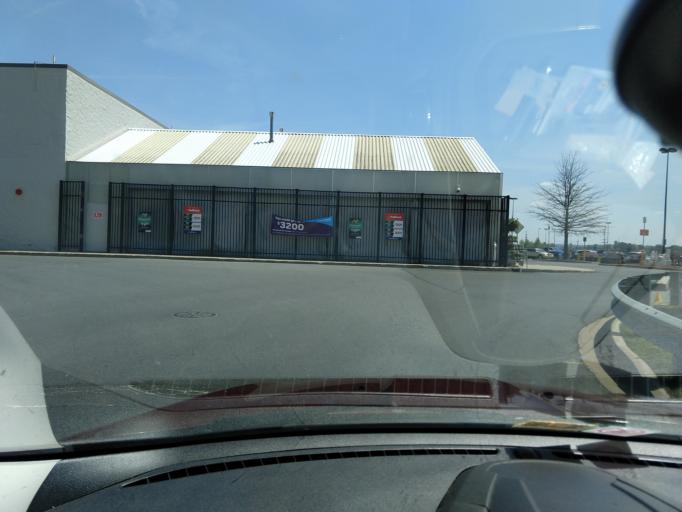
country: US
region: West Virginia
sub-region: Raleigh County
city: Stanaford
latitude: 37.8061
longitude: -81.1782
